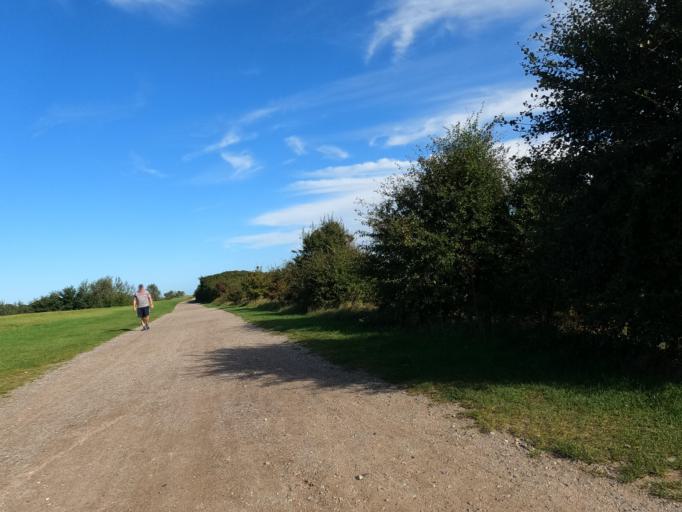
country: DE
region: Schleswig-Holstein
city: Dahme
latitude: 54.2759
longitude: 11.0831
